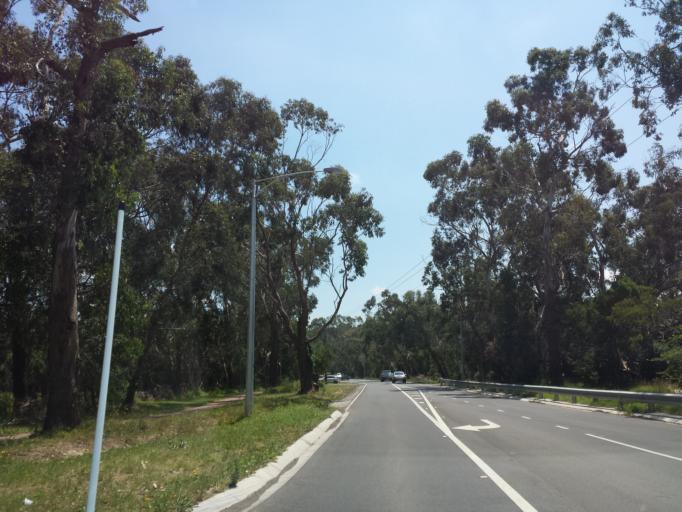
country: AU
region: Victoria
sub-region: Knox
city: The Basin
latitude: -37.8410
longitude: 145.3185
